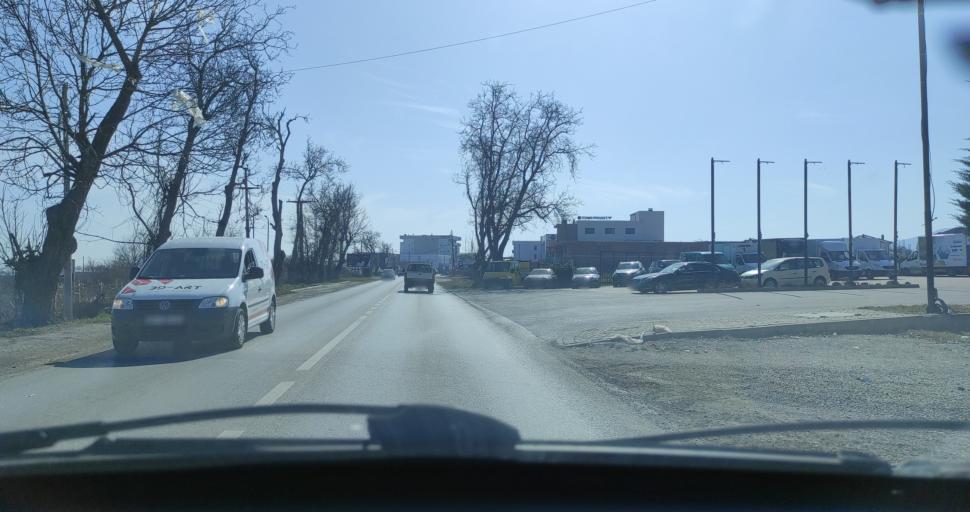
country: XK
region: Pec
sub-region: Komuna e Pejes
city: Peje
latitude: 42.6308
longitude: 20.3041
